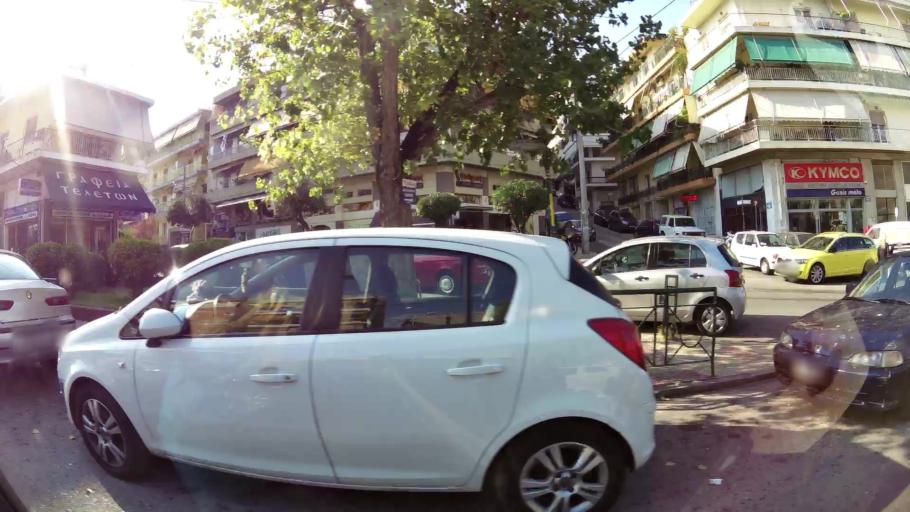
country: GR
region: Attica
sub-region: Nomarchia Athinas
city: Galatsi
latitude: 38.0203
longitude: 23.7522
